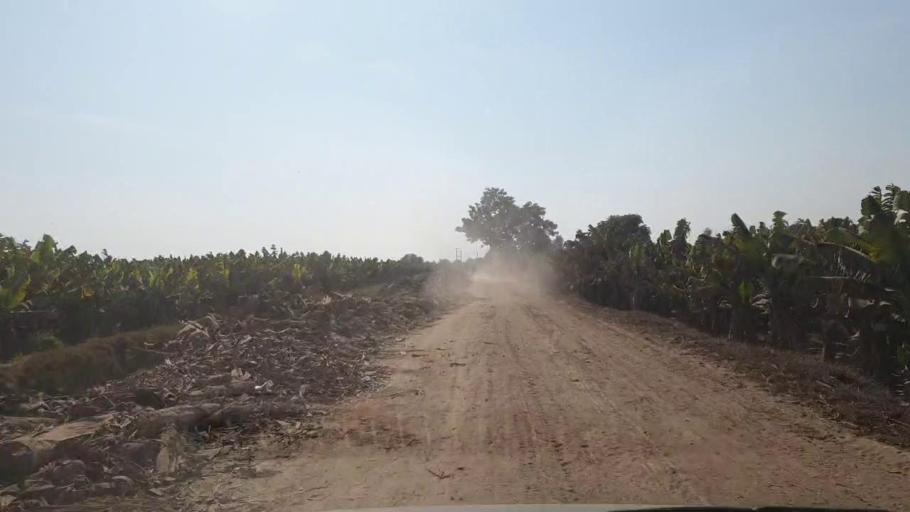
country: PK
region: Sindh
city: Chambar
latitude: 25.3722
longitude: 68.8078
